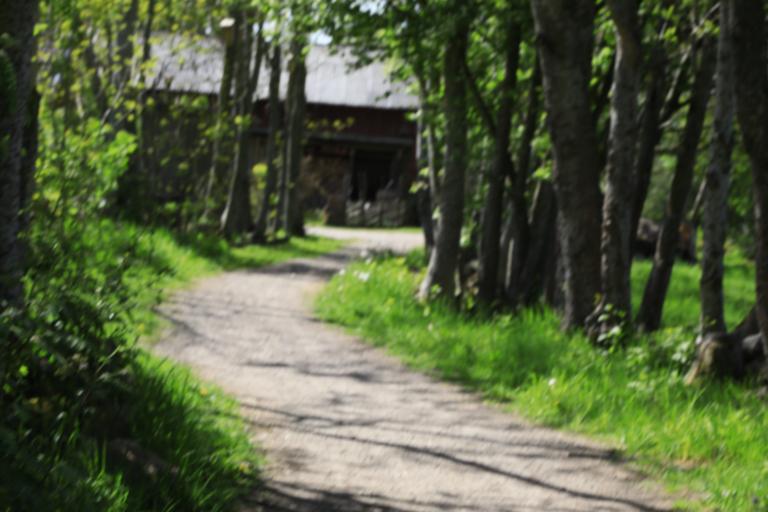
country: SE
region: Halland
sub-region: Varbergs Kommun
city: Varberg
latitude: 57.1139
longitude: 12.2982
